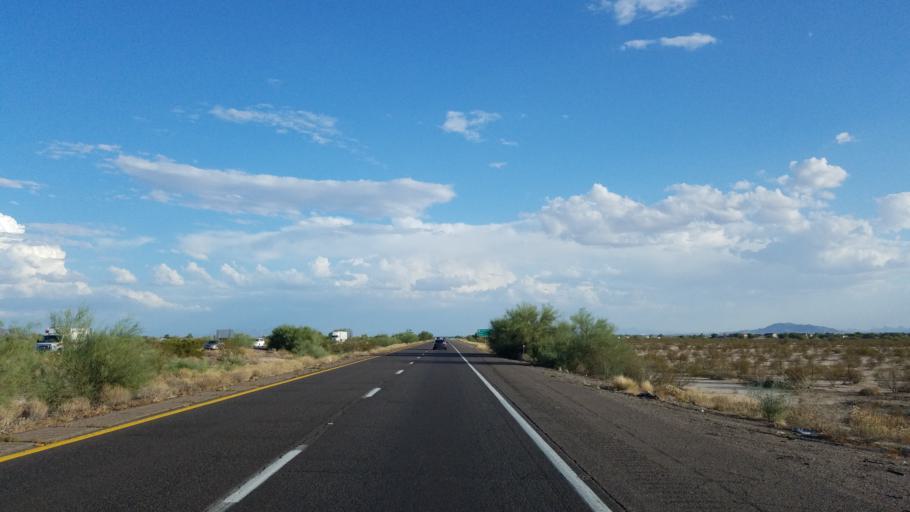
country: US
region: Arizona
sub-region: Pinal County
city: Sacaton
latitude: 32.9913
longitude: -111.7438
